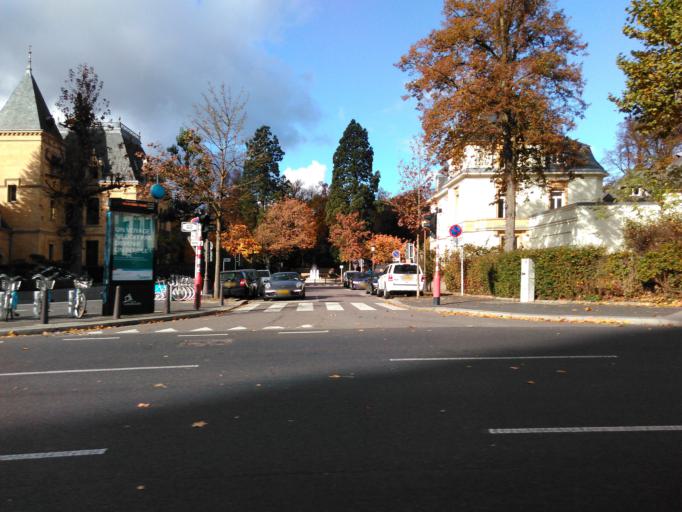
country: LU
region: Luxembourg
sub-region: Canton de Luxembourg
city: Luxembourg
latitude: 49.6133
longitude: 6.1260
